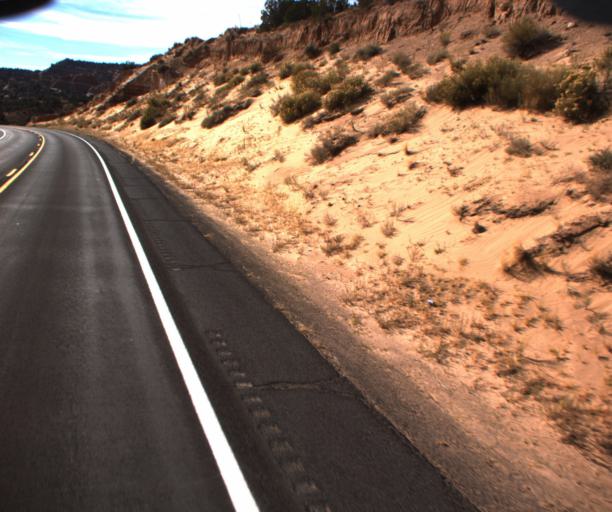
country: US
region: Arizona
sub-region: Coconino County
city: Kaibito
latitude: 36.6063
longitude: -110.9207
